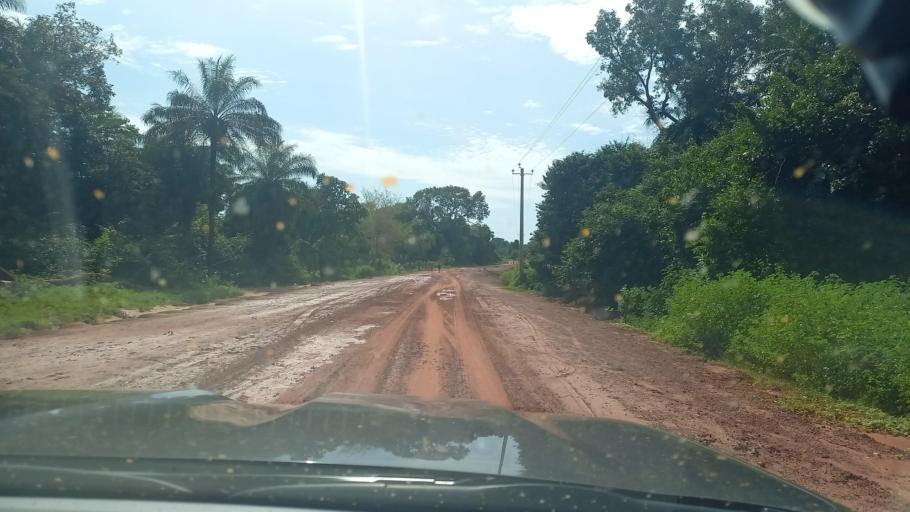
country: SN
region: Ziguinchor
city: Ziguinchor
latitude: 12.6733
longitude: -16.1920
